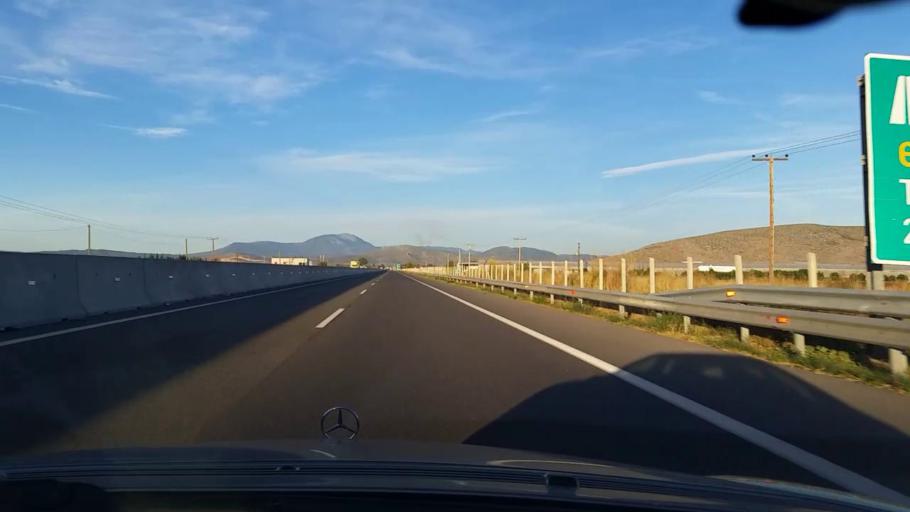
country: GR
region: Central Greece
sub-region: Nomos Voiotias
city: Thivai
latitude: 38.3676
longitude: 23.3507
